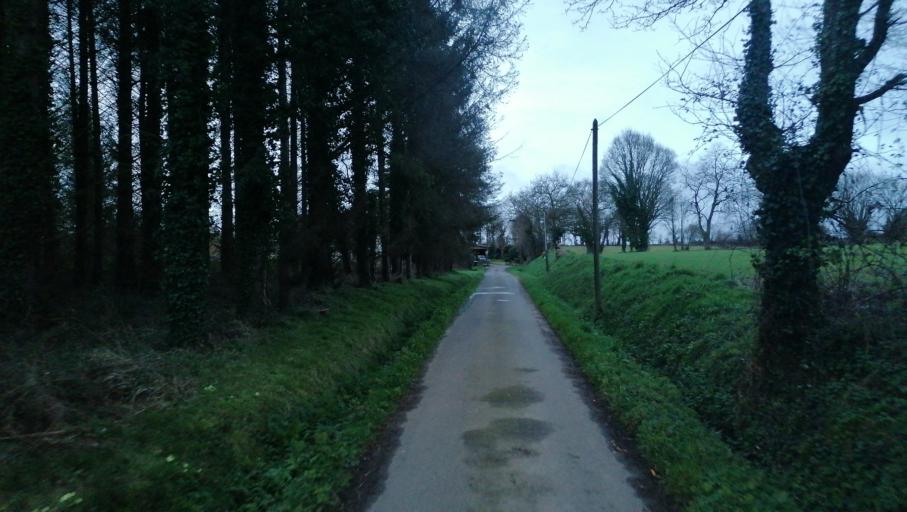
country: FR
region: Brittany
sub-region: Departement des Cotes-d'Armor
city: Goudelin
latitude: 48.5783
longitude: -3.0578
